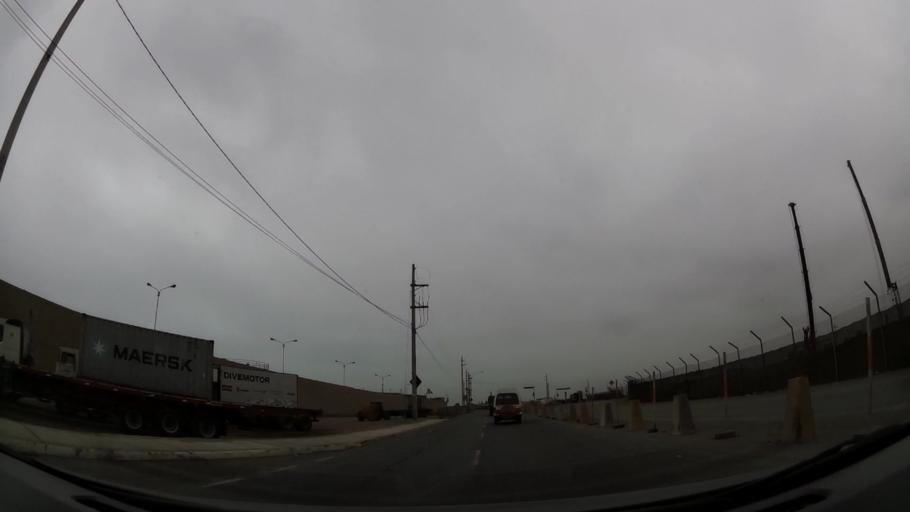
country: PE
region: Callao
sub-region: Callao
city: Callao
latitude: -12.0211
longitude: -77.1297
